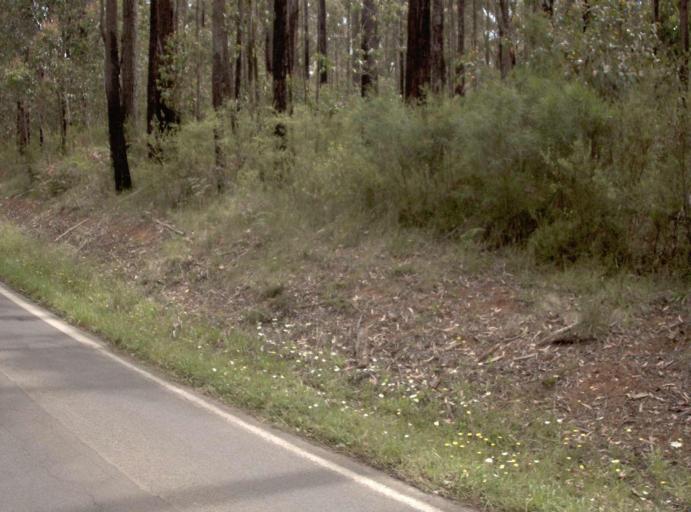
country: AU
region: Victoria
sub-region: Latrobe
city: Traralgon
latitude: -38.0233
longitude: 146.4175
